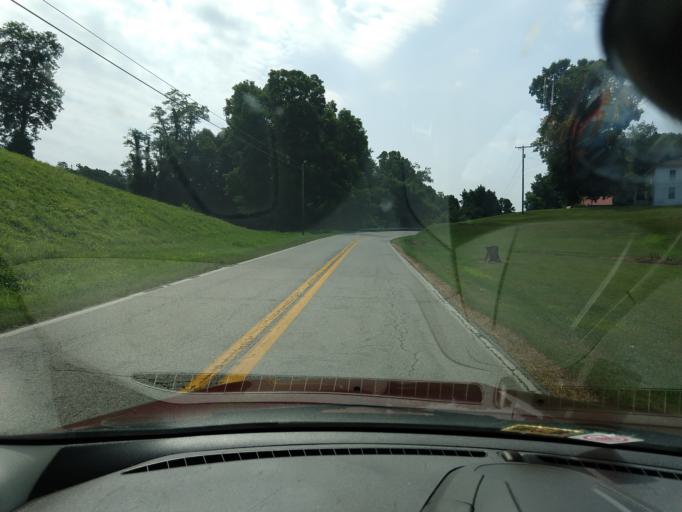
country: US
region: West Virginia
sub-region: Mason County
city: New Haven
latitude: 38.9353
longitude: -81.9179
